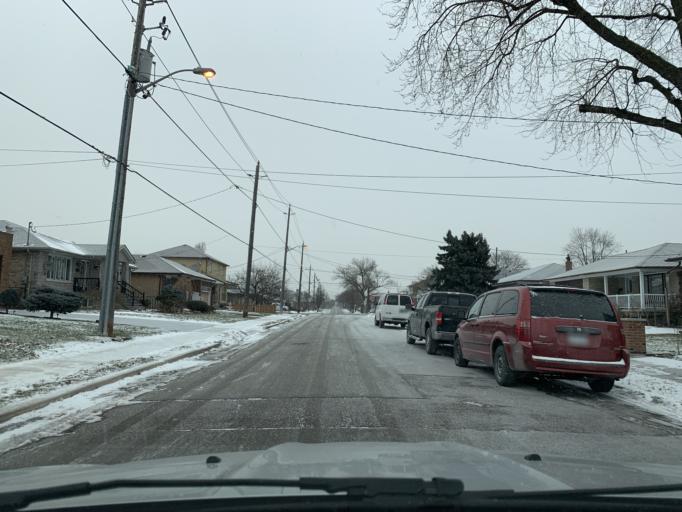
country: CA
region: Ontario
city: Toronto
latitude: 43.7309
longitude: -79.4696
